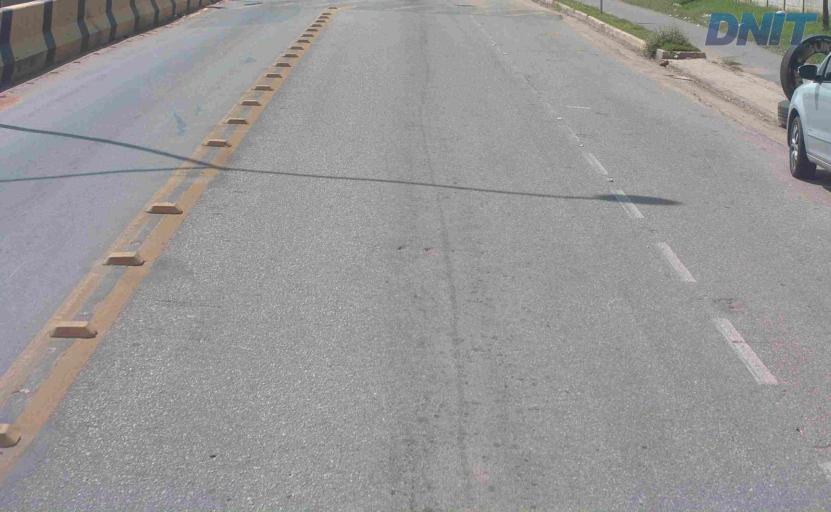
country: BR
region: Minas Gerais
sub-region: Governador Valadares
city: Governador Valadares
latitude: -18.9044
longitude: -41.9892
